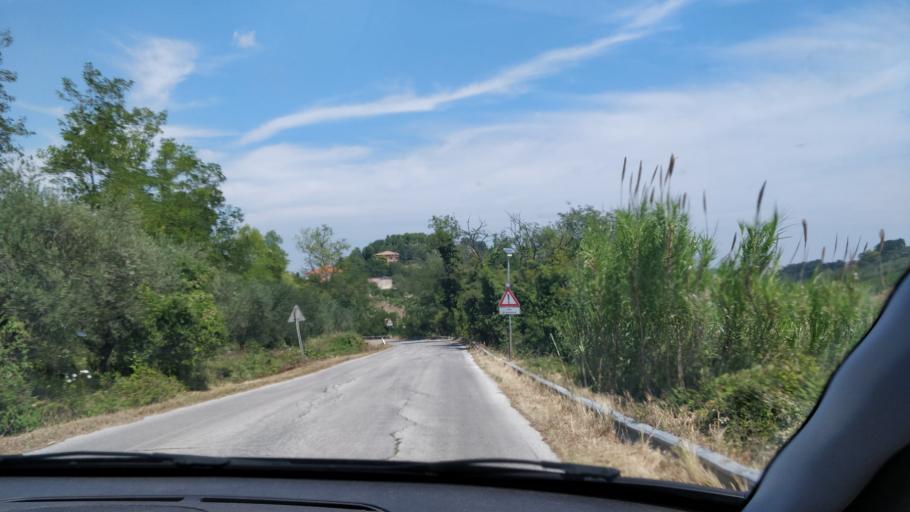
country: IT
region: Abruzzo
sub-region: Provincia di Chieti
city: Torrevecchia
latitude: 42.3996
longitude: 14.2052
